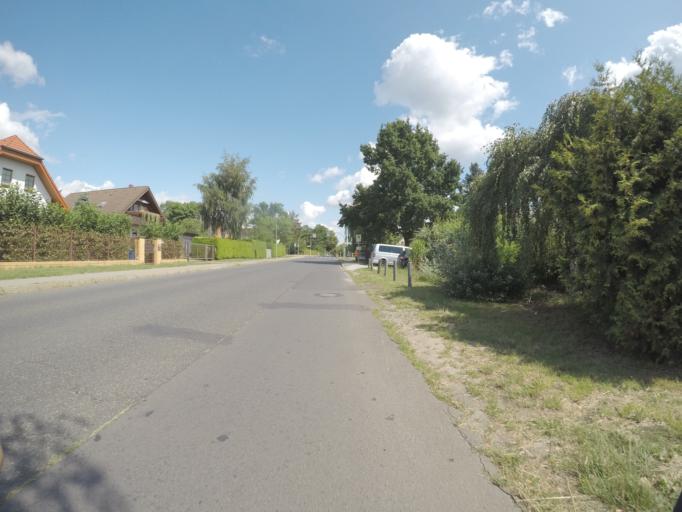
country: DE
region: Berlin
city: Kaulsdorf
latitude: 52.5028
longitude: 13.5860
